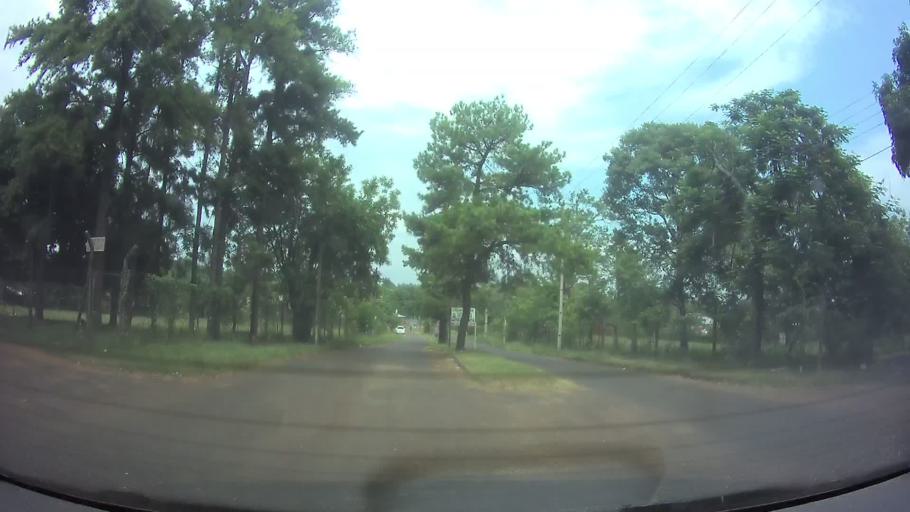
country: PY
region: Central
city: Fernando de la Mora
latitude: -25.2908
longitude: -57.5118
